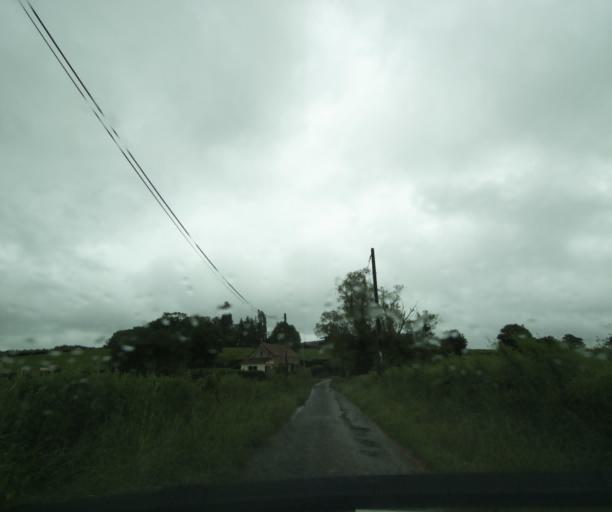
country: FR
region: Bourgogne
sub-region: Departement de Saone-et-Loire
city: Charolles
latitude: 46.5067
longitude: 4.3805
